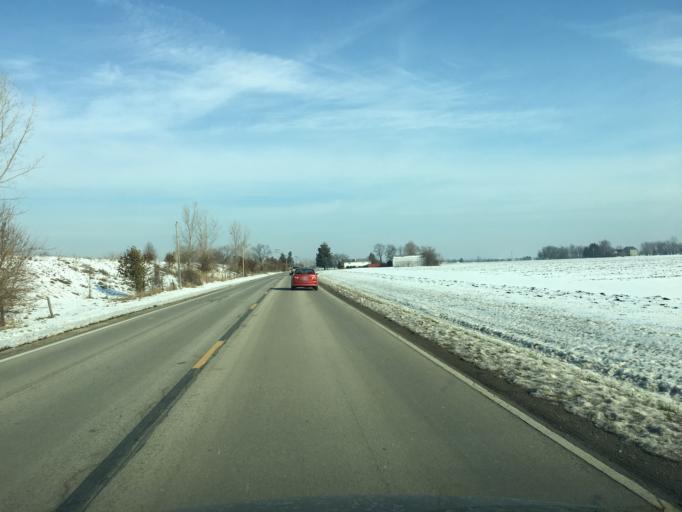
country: US
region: Illinois
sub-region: Will County
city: Plainfield
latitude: 41.6740
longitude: -88.1723
